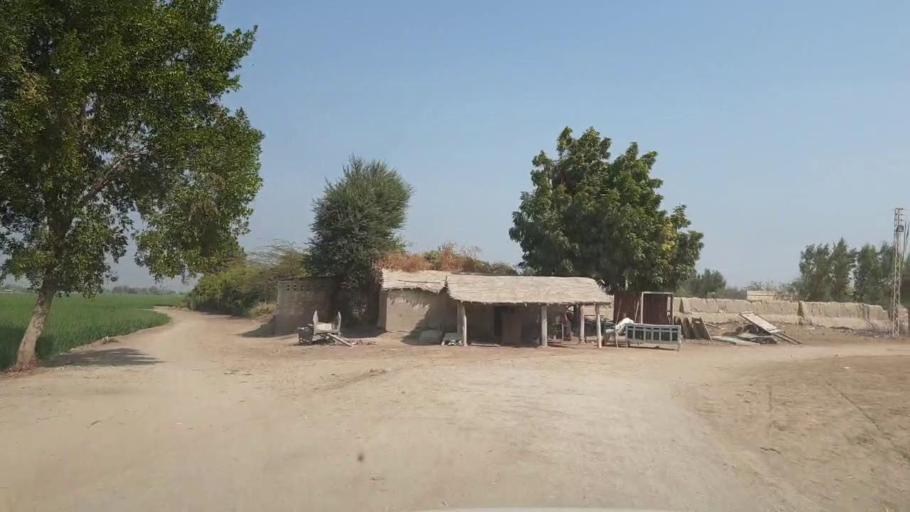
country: PK
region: Sindh
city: Mirpur Khas
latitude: 25.6514
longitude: 69.1531
